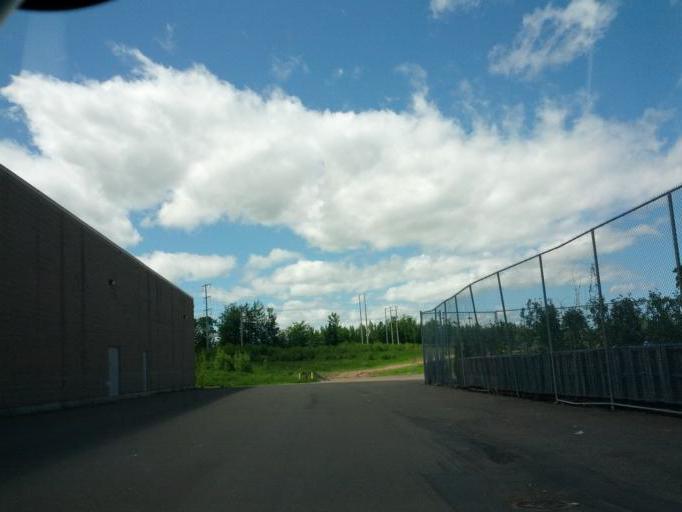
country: CA
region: New Brunswick
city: Moncton
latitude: 46.1186
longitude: -64.8316
